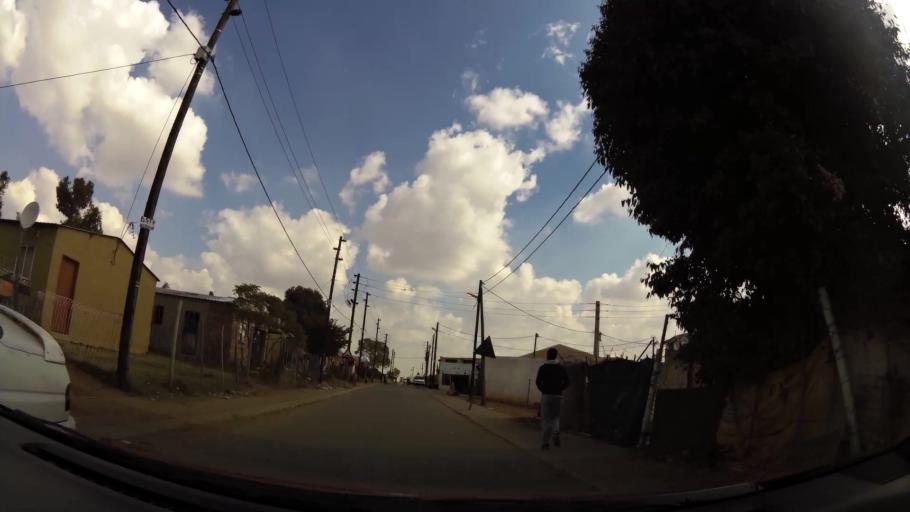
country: ZA
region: Gauteng
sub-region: City of Johannesburg Metropolitan Municipality
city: Roodepoort
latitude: -26.1838
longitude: 27.8508
